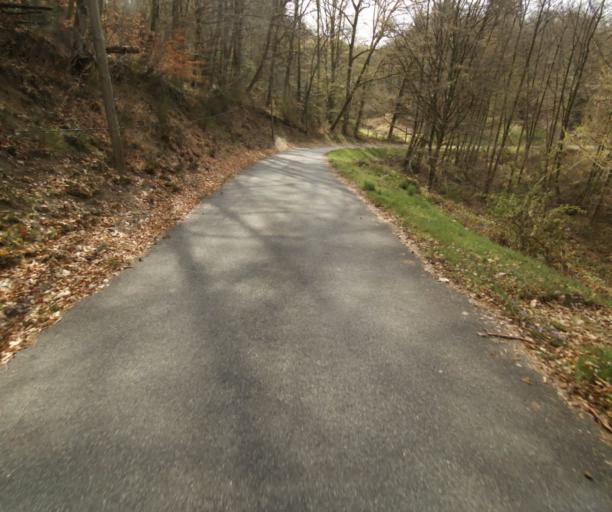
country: FR
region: Limousin
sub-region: Departement de la Correze
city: Correze
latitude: 45.3438
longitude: 1.8592
